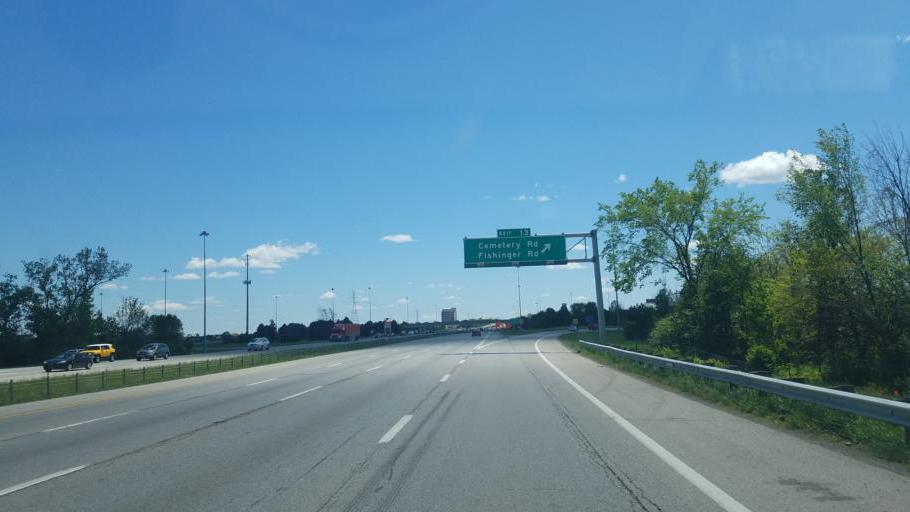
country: US
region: Ohio
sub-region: Franklin County
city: Hilliard
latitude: 40.0379
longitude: -83.1254
